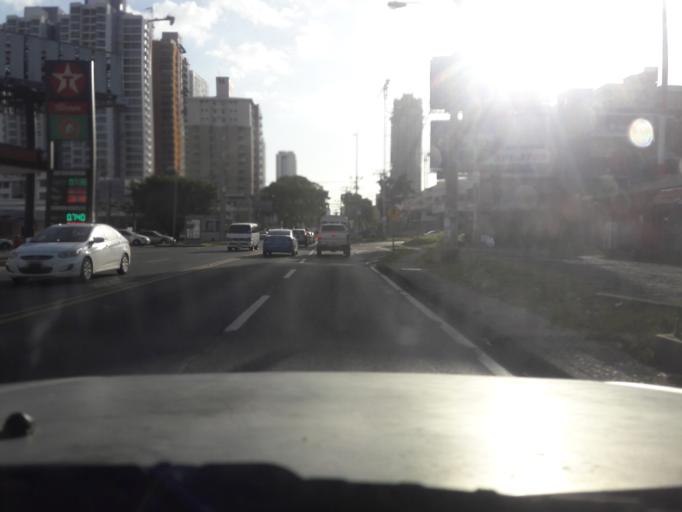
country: PA
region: Panama
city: Panama
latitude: 9.0092
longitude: -79.5067
